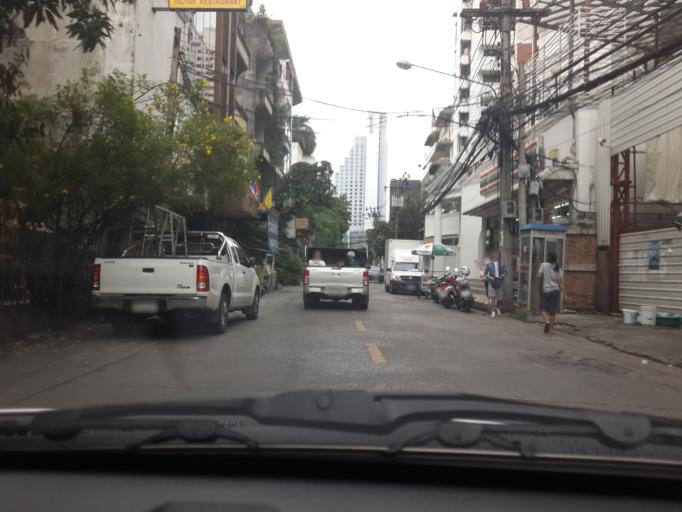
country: TH
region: Bangkok
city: Khlong Toei
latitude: 13.7304
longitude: 100.5638
